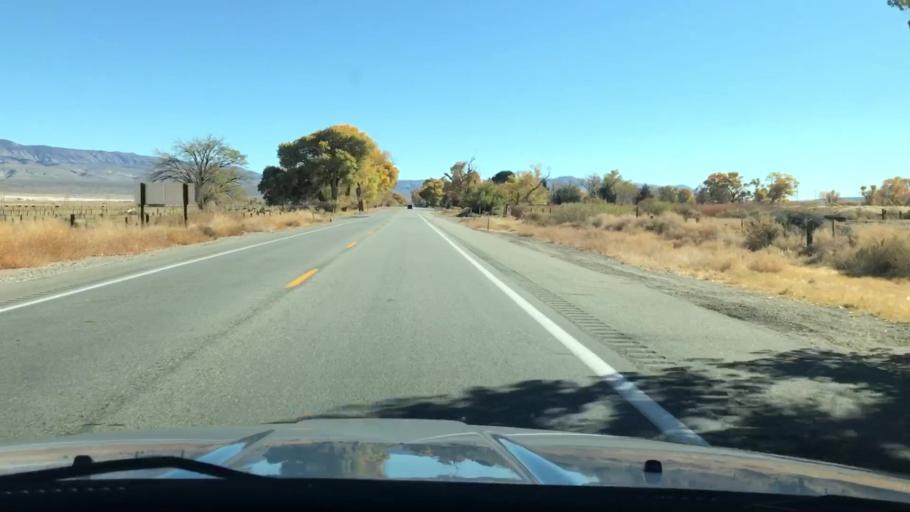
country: US
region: California
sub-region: Inyo County
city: Lone Pine
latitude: 36.2906
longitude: -118.0148
